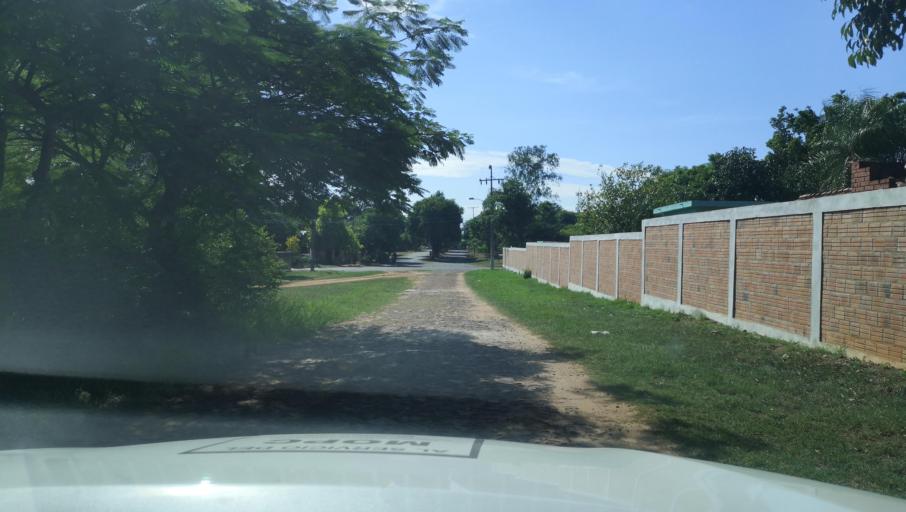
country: PY
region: Misiones
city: Santa Maria
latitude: -26.8928
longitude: -57.0321
